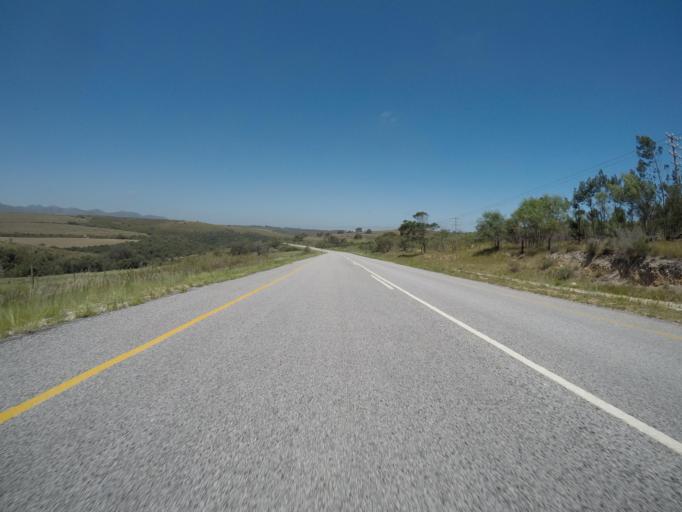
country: ZA
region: Eastern Cape
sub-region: Cacadu District Municipality
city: Kruisfontein
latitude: -34.0194
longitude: 24.5774
